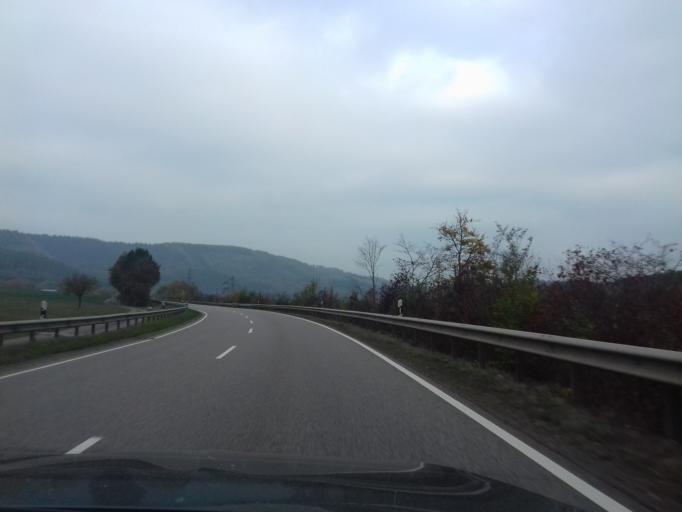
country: DE
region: Rheinland-Pfalz
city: Ayl
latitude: 49.6386
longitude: 6.5471
